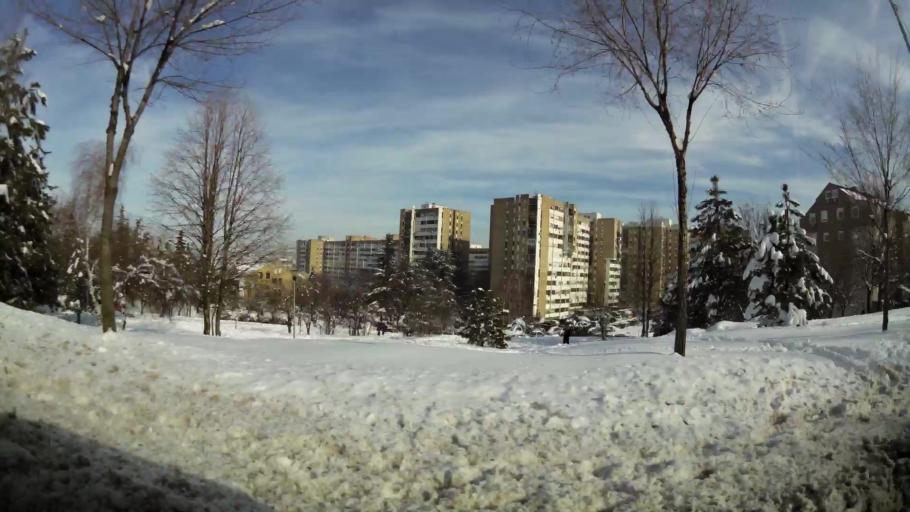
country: RS
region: Central Serbia
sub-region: Belgrade
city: Zvezdara
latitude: 44.7866
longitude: 20.5281
